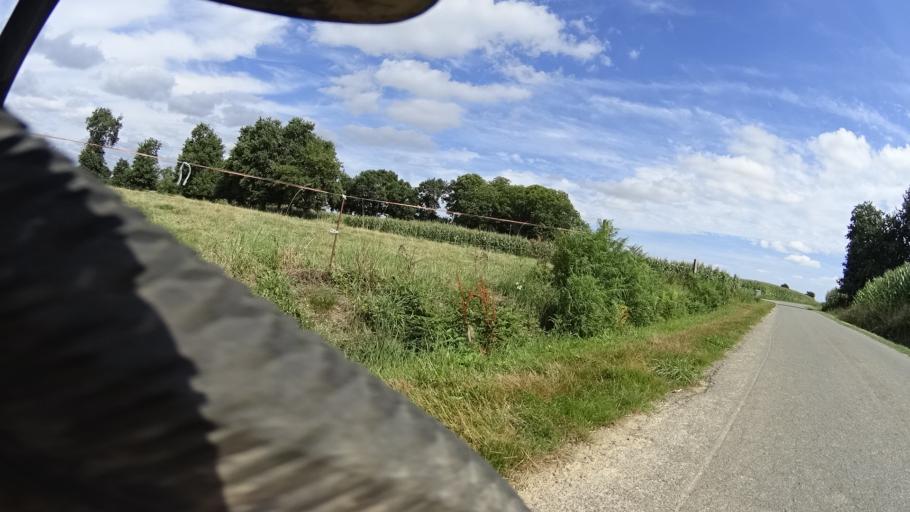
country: FR
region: Brittany
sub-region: Departement d'Ille-et-Vilaine
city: Vignoc
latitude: 48.2347
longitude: -1.7752
